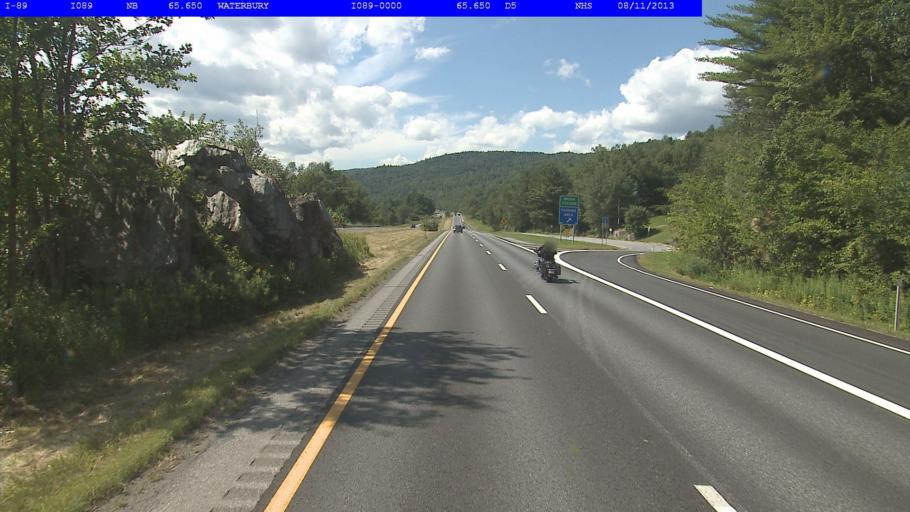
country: US
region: Vermont
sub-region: Washington County
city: Waterbury
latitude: 44.3547
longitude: -72.7858
